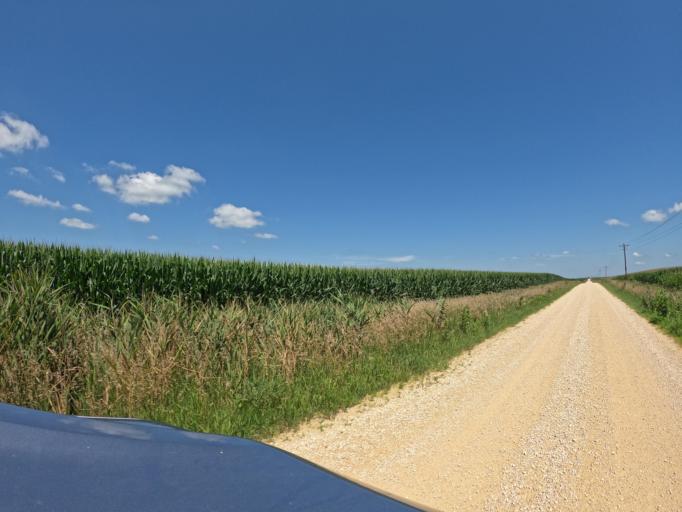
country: US
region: Iowa
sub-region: Clinton County
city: Camanche
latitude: 41.7741
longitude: -90.3936
